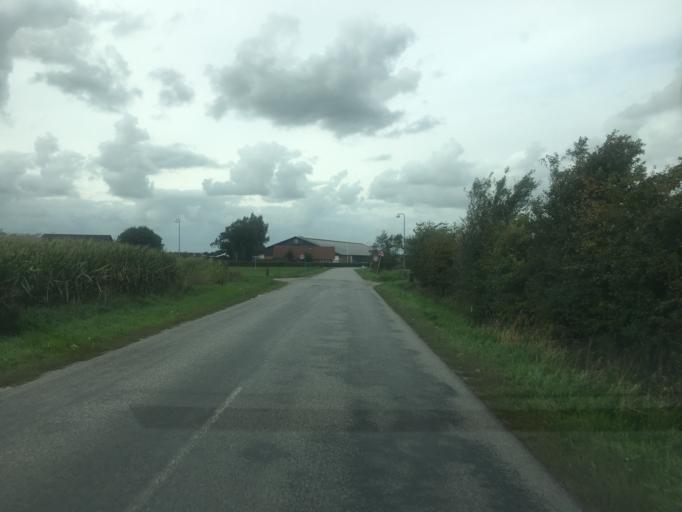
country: DE
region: Schleswig-Holstein
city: Aventoft
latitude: 54.9540
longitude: 8.8012
